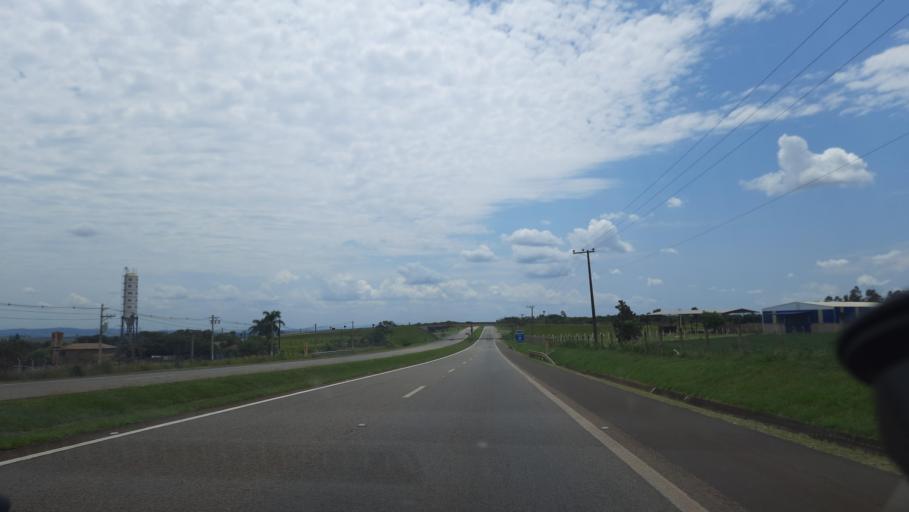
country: BR
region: Sao Paulo
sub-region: Casa Branca
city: Casa Branca
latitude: -21.7518
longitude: -47.0714
